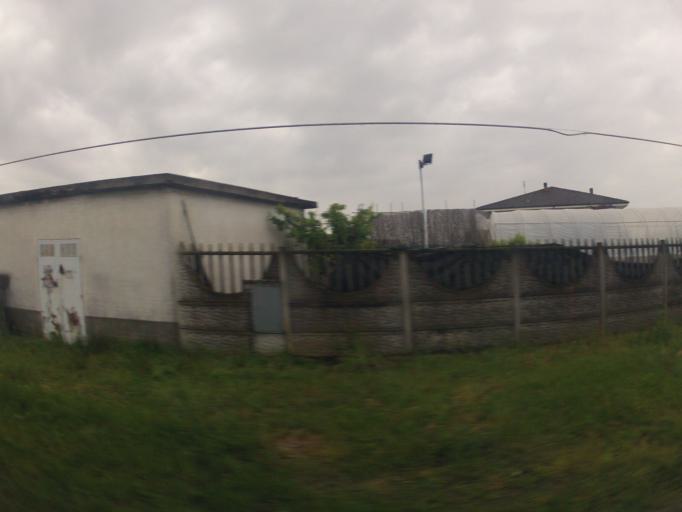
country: IT
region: Piedmont
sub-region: Provincia di Cuneo
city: Polonghera
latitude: 44.8055
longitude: 7.6052
